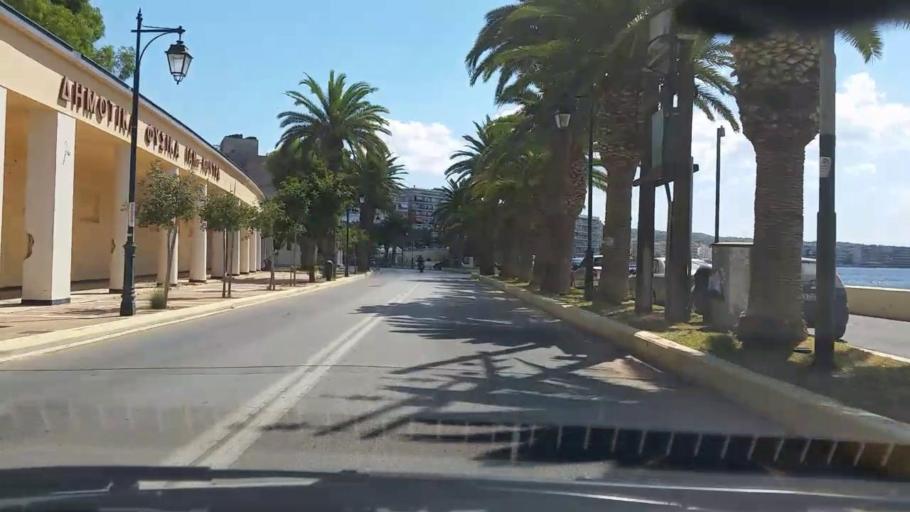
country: GR
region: Peloponnese
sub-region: Nomos Korinthias
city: Loutraki
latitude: 37.9828
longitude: 22.9698
